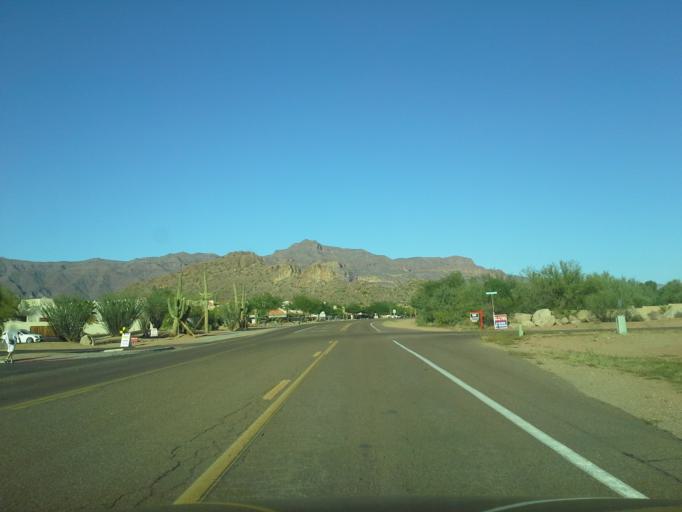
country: US
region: Arizona
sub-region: Pinal County
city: Apache Junction
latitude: 33.3572
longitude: -111.4519
